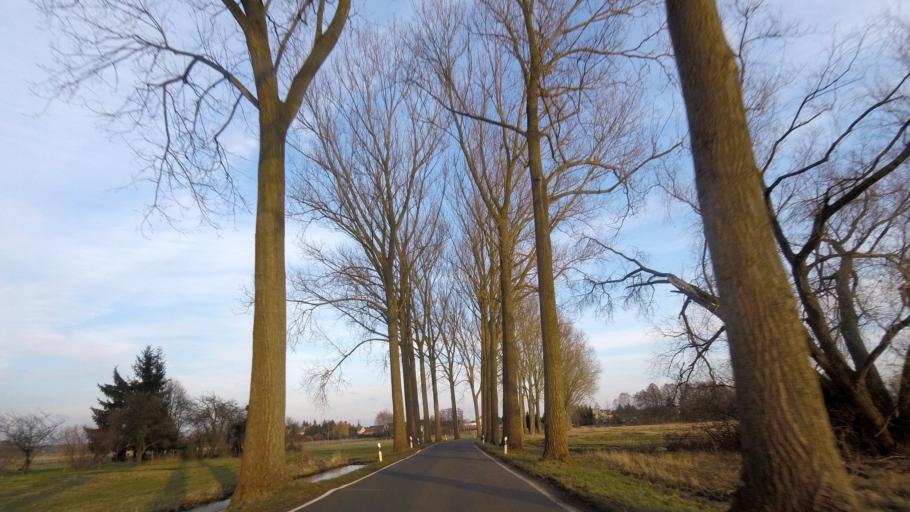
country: DE
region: Brandenburg
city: Niemegk
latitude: 52.0780
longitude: 12.6824
